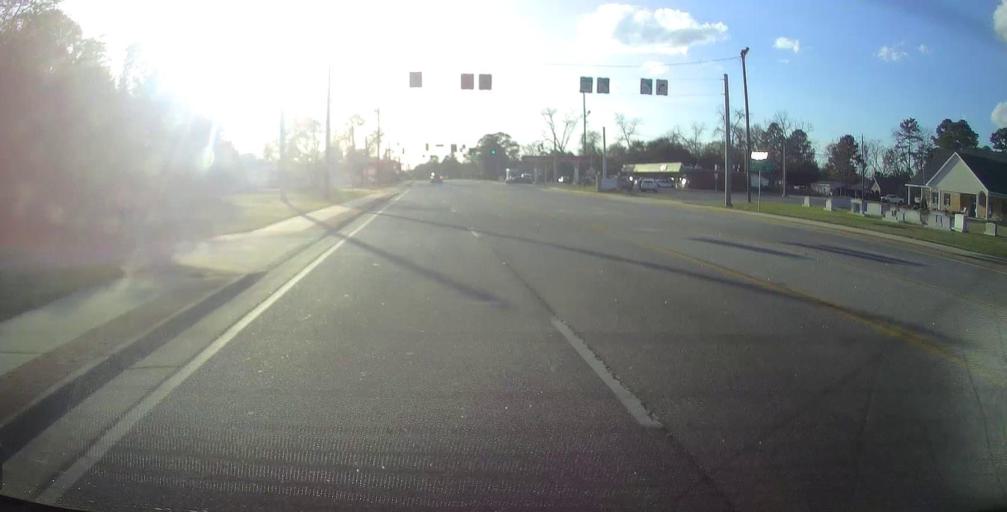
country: US
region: Georgia
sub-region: Evans County
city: Claxton
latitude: 32.1610
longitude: -81.9126
